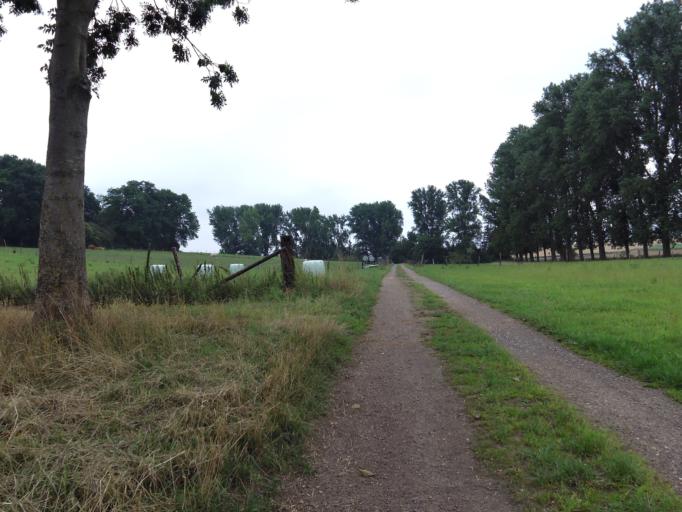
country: DE
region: North Rhine-Westphalia
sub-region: Regierungsbezirk Koln
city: Linnich
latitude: 50.9687
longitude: 6.2579
